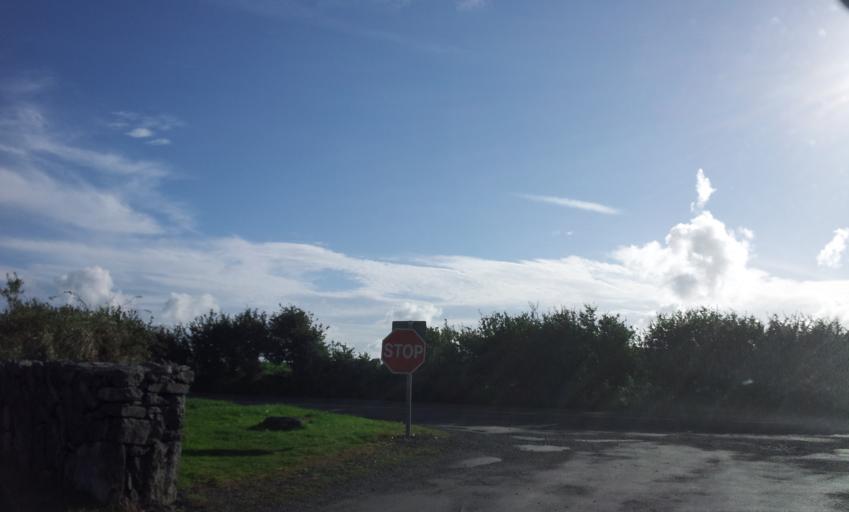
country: IE
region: Connaught
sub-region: County Galway
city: Bearna
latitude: 53.0470
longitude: -9.1406
